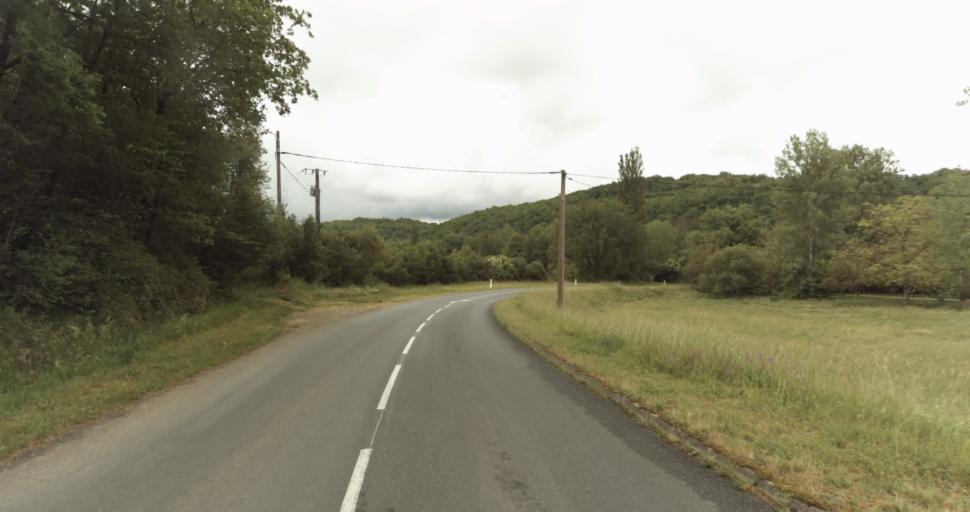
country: FR
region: Aquitaine
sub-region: Departement de la Dordogne
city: Beaumont-du-Perigord
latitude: 44.7702
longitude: 0.7963
